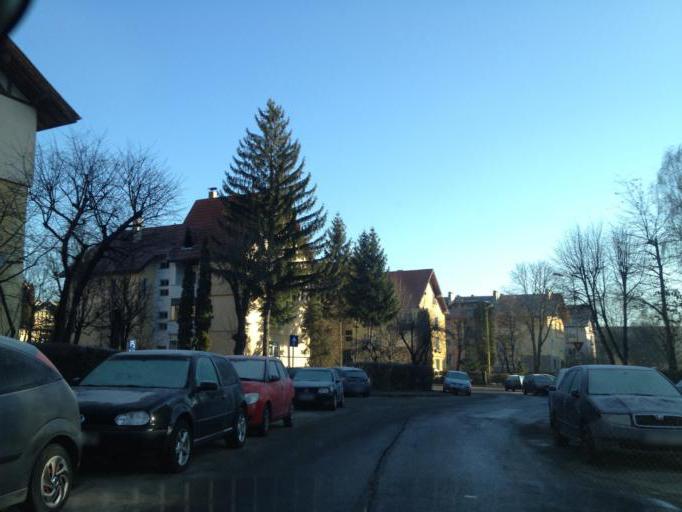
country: RO
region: Brasov
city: Brasov
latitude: 45.6381
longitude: 25.6302
